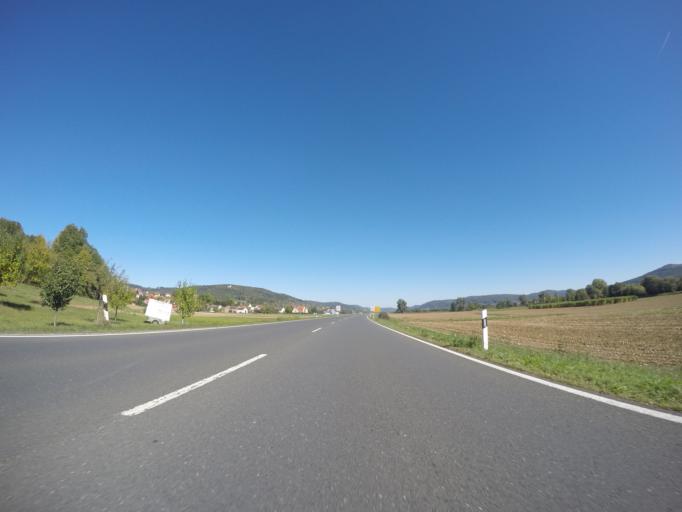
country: DE
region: Bavaria
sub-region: Upper Franconia
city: Kirchehrenbach
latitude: 49.7378
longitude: 11.1322
